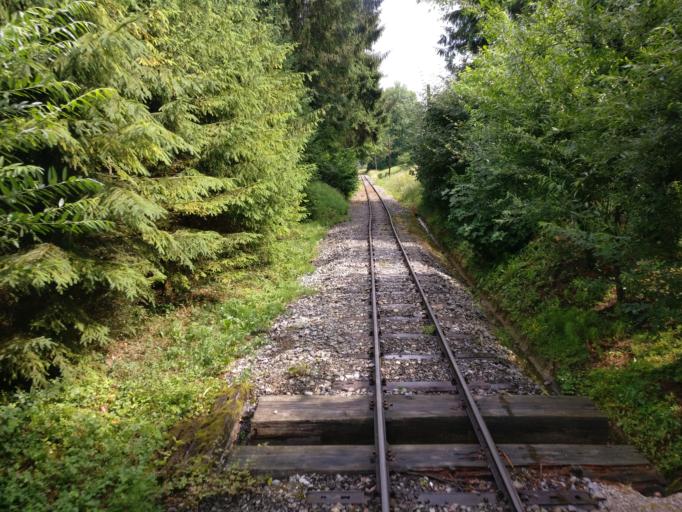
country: AT
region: Upper Austria
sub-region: Politischer Bezirk Steyr-Land
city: Sierning
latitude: 48.0279
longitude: 14.3356
